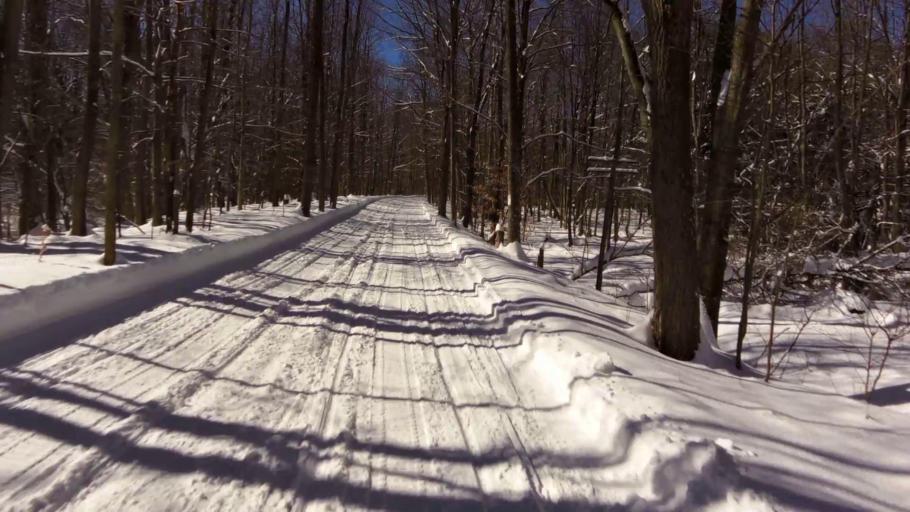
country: US
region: New York
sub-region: Chautauqua County
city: Mayville
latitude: 42.2352
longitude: -79.5051
